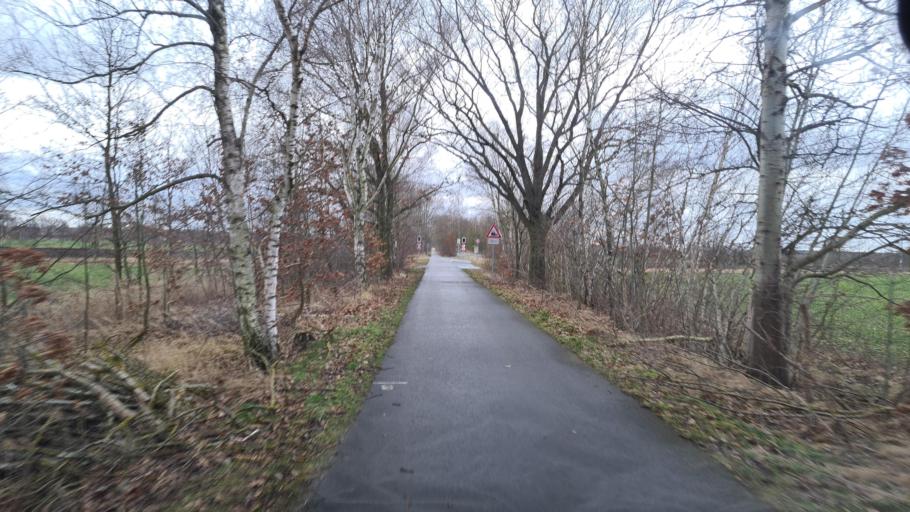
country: DE
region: Brandenburg
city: Kroppen
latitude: 51.3962
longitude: 13.7877
